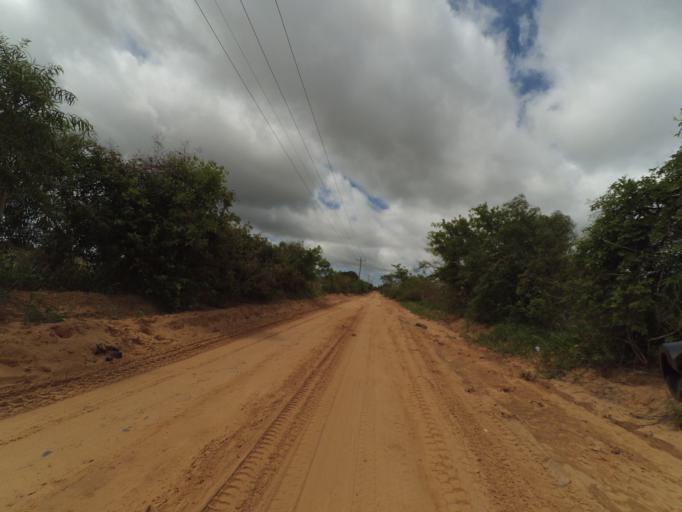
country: BO
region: Santa Cruz
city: Santa Rita
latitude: -17.9094
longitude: -63.2477
